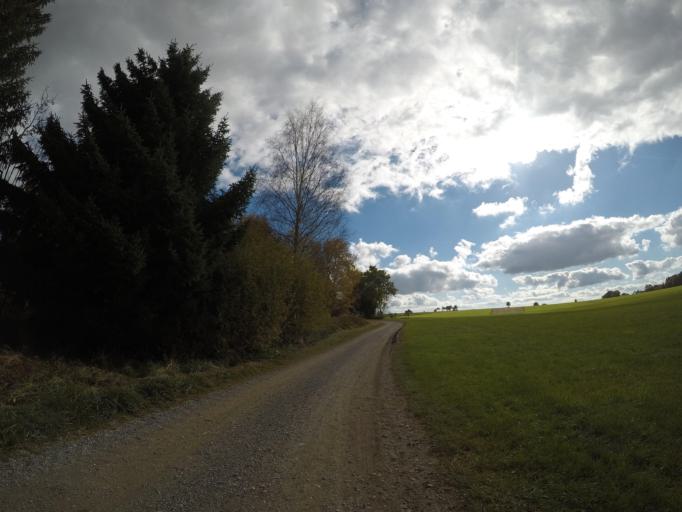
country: DE
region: Baden-Wuerttemberg
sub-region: Tuebingen Region
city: Tiefenbach
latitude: 48.0835
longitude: 9.6470
